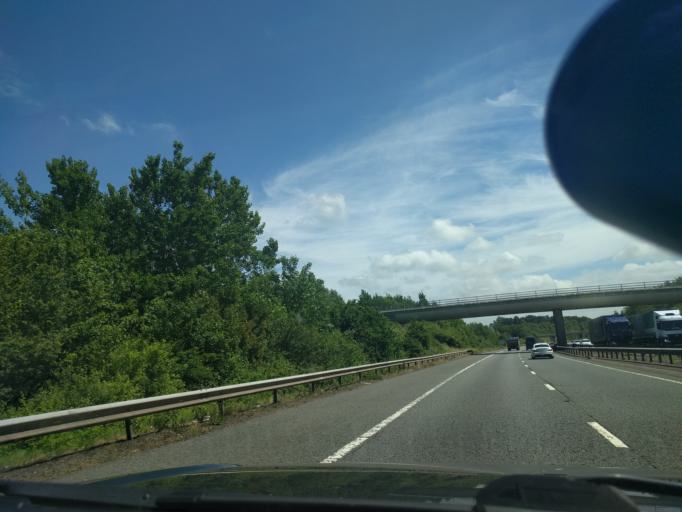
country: GB
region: England
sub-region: South Gloucestershire
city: Almondsbury
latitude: 51.5754
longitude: -2.5920
